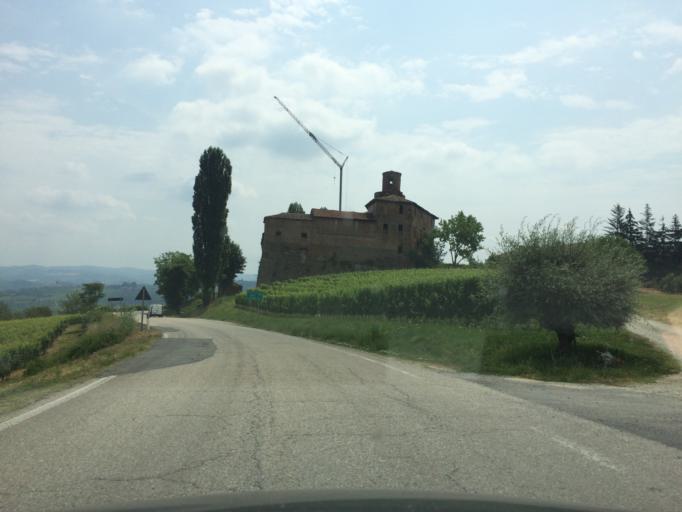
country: IT
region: Piedmont
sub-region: Provincia di Cuneo
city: Barolo
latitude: 44.6146
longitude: 7.9340
